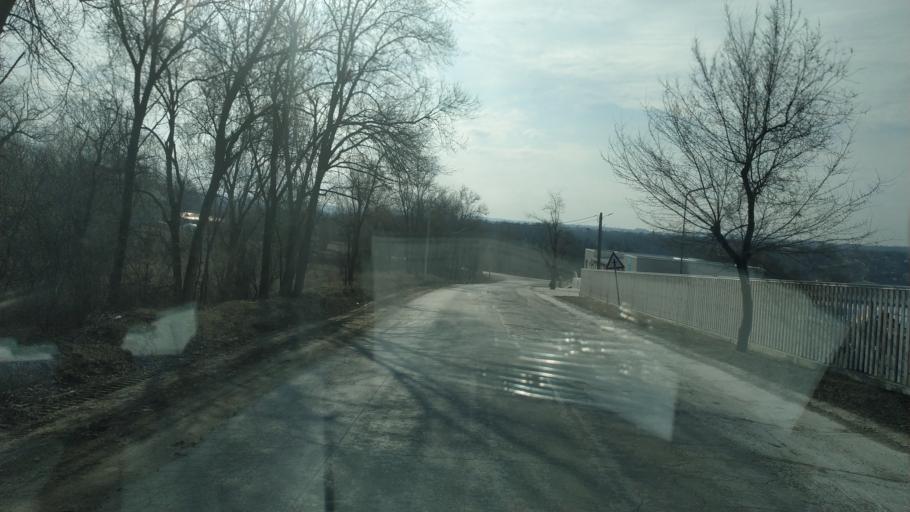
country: MD
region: Chisinau
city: Singera
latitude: 46.9281
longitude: 29.0488
